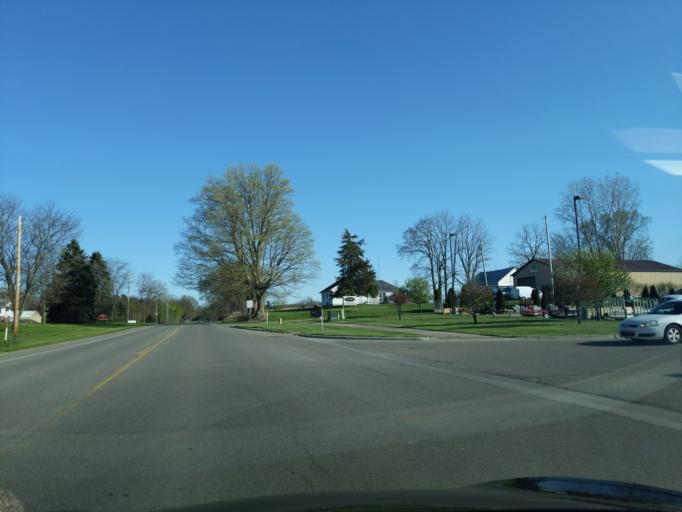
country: US
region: Michigan
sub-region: Ionia County
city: Portland
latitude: 42.8566
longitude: -84.8820
